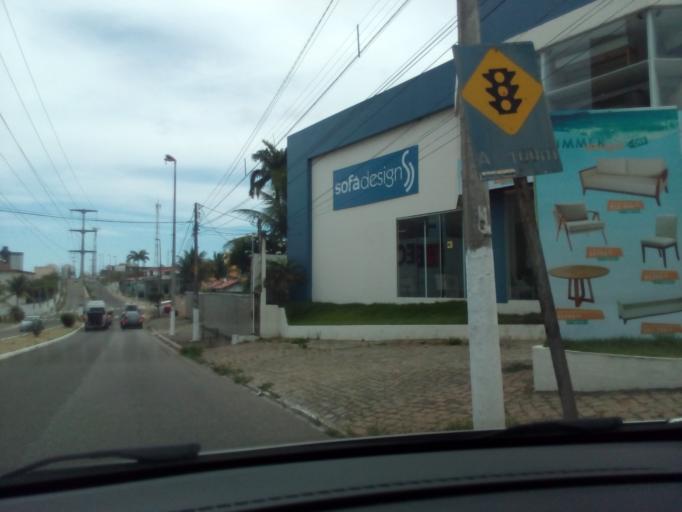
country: BR
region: Rio Grande do Norte
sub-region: Natal
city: Natal
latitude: -5.8448
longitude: -35.2176
